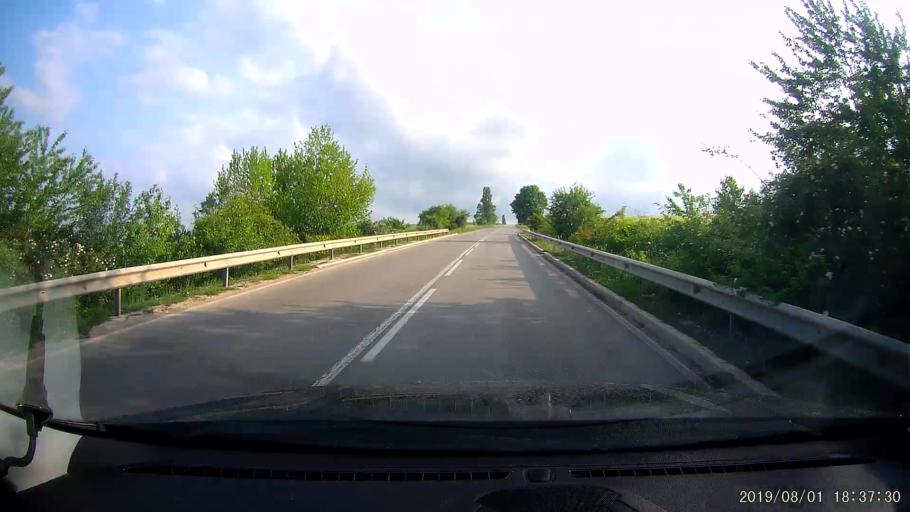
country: BG
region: Shumen
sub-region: Obshtina Khitrino
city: Gara Khitrino
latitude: 43.4199
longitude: 26.9298
